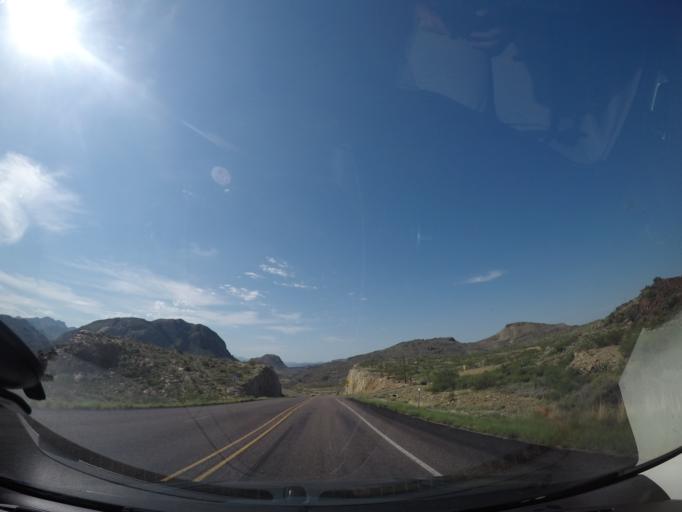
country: US
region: Texas
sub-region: Presidio County
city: Presidio
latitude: 29.4499
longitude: -103.5136
